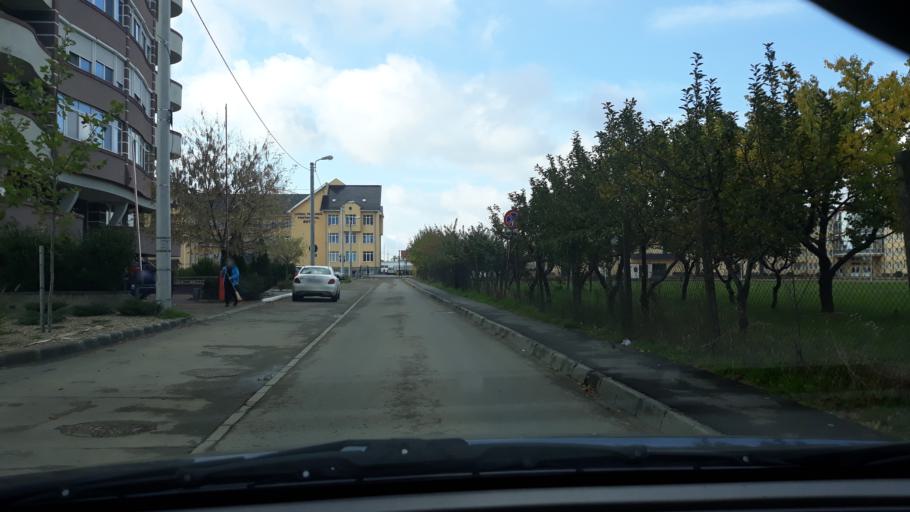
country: RO
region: Bihor
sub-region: Comuna Sanmartin
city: Sanmartin
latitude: 47.0276
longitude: 21.9530
